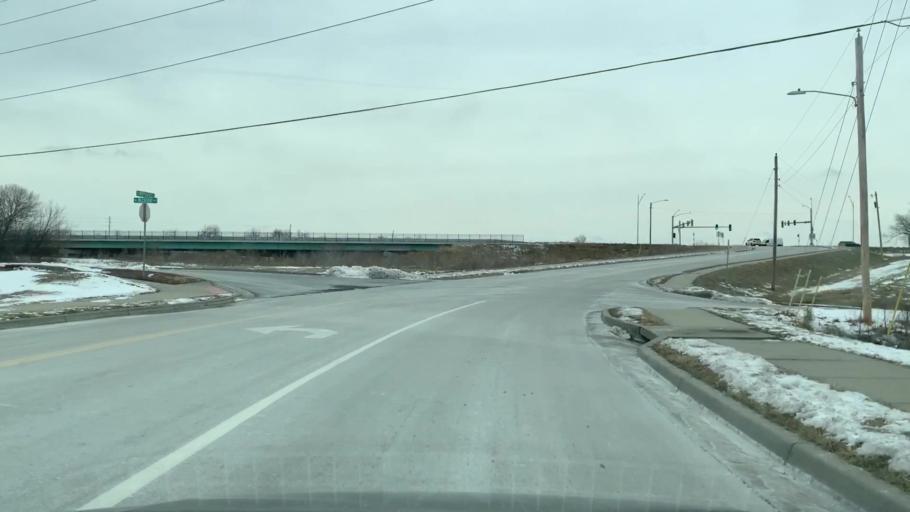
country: US
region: Missouri
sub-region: Jackson County
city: Lees Summit
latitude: 38.9447
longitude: -94.3642
